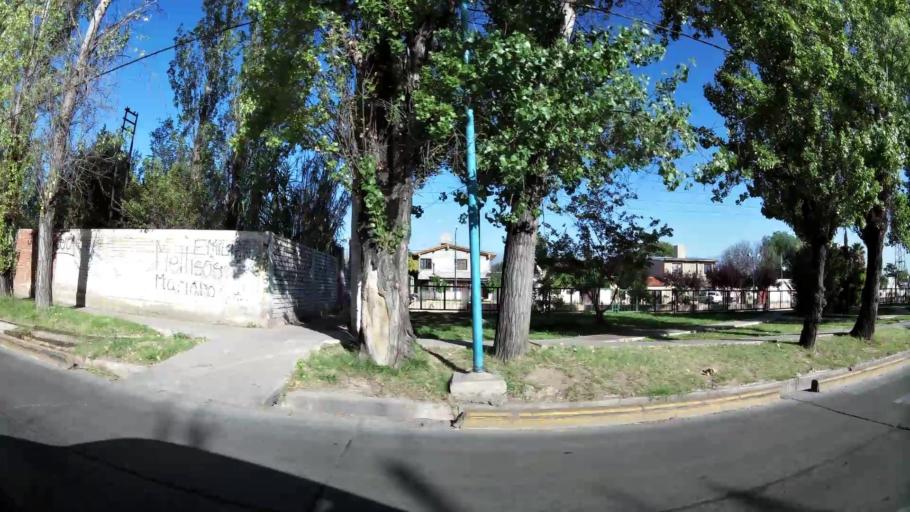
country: AR
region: Mendoza
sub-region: Departamento de Godoy Cruz
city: Godoy Cruz
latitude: -32.9321
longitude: -68.8395
